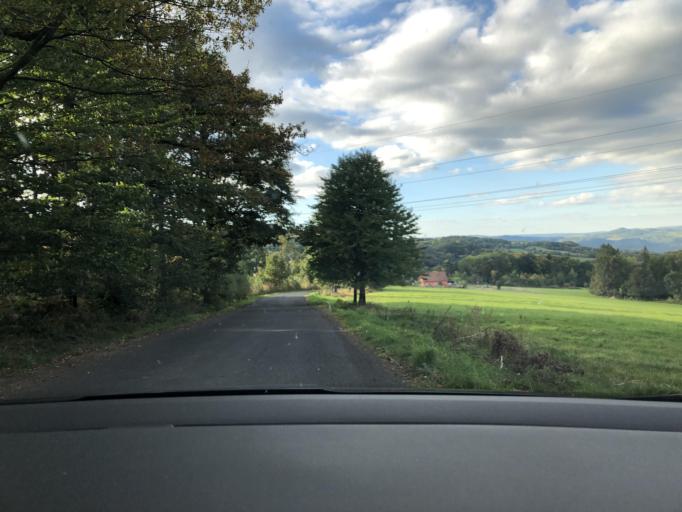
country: CZ
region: Ustecky
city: Velke Brezno
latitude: 50.6219
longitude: 14.1619
